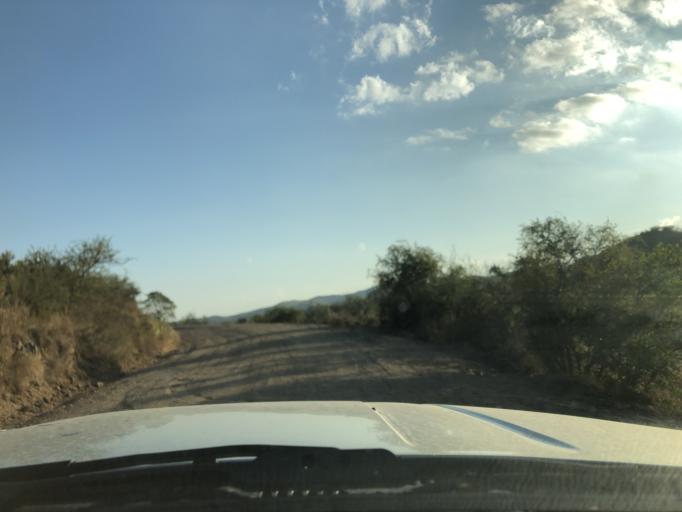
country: AR
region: Cordoba
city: Agua de Oro
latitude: -31.0562
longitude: -64.3508
